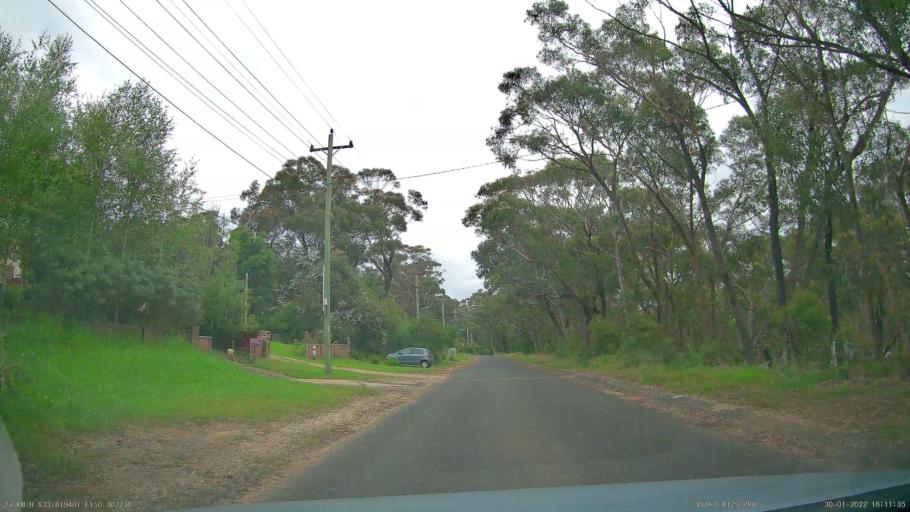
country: AU
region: New South Wales
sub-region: Blue Mountains Municipality
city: Blackheath
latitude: -33.6195
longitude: 150.3021
